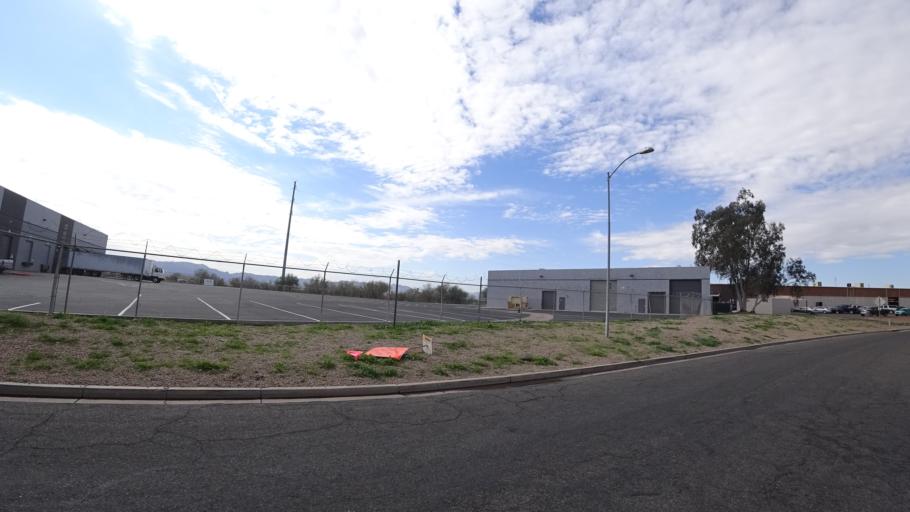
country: US
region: Arizona
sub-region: Maricopa County
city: Phoenix
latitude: 33.4233
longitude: -112.0685
